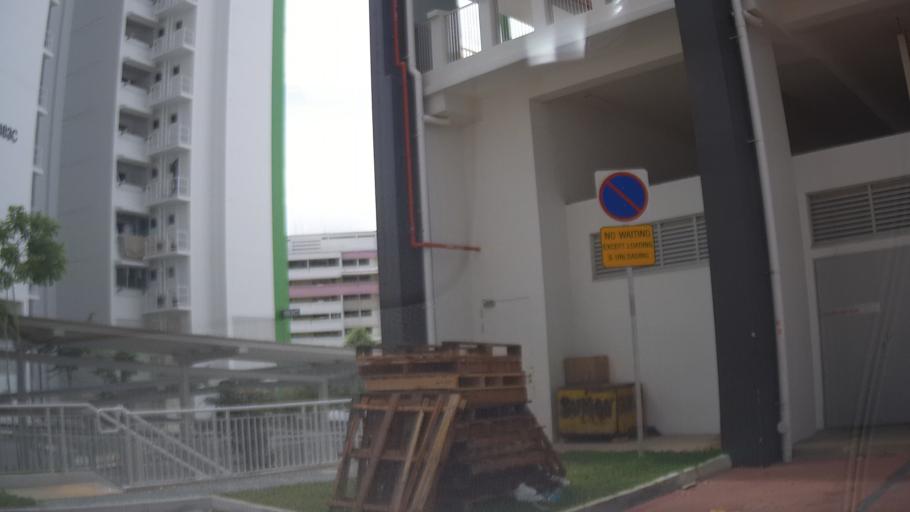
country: MY
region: Johor
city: Johor Bahru
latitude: 1.4355
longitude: 103.7764
